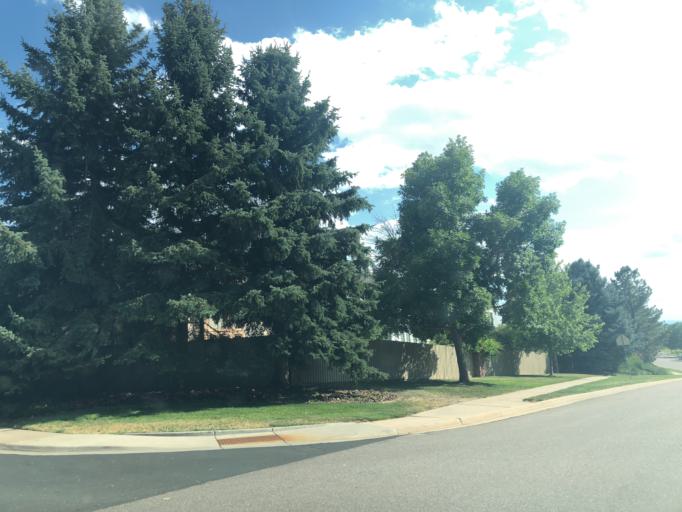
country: US
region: Colorado
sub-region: Arapahoe County
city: Dove Valley
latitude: 39.6104
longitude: -104.7676
